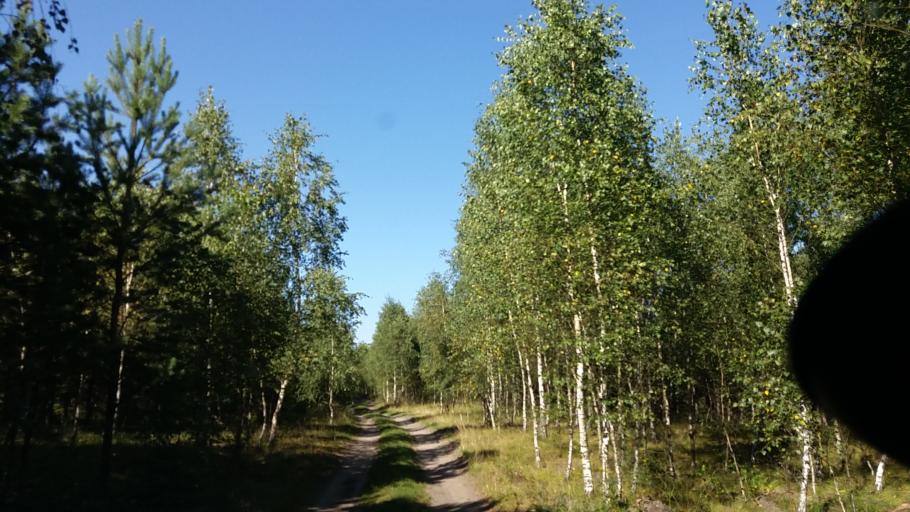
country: PL
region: West Pomeranian Voivodeship
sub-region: Powiat szczecinecki
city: Borne Sulinowo
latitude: 53.5804
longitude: 16.5234
